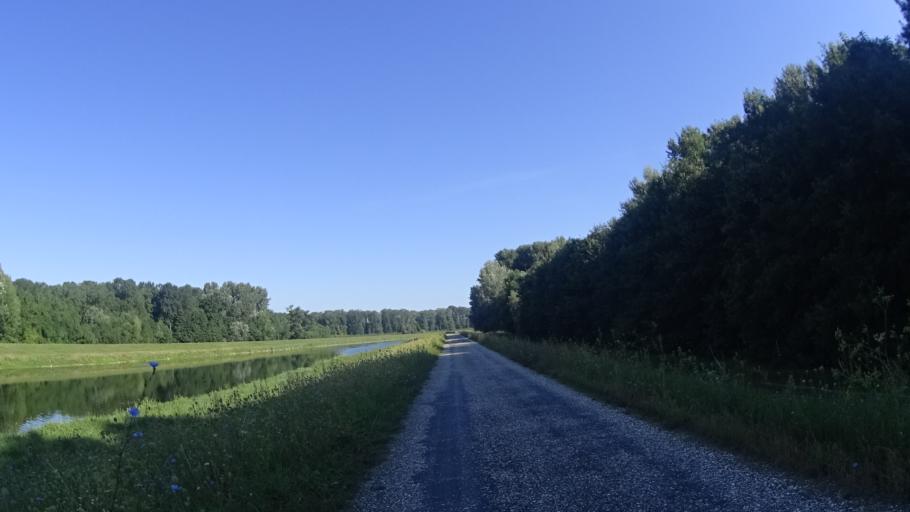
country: CZ
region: South Moravian
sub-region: Okres Breclav
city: Lanzhot
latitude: 48.7022
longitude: 16.9982
